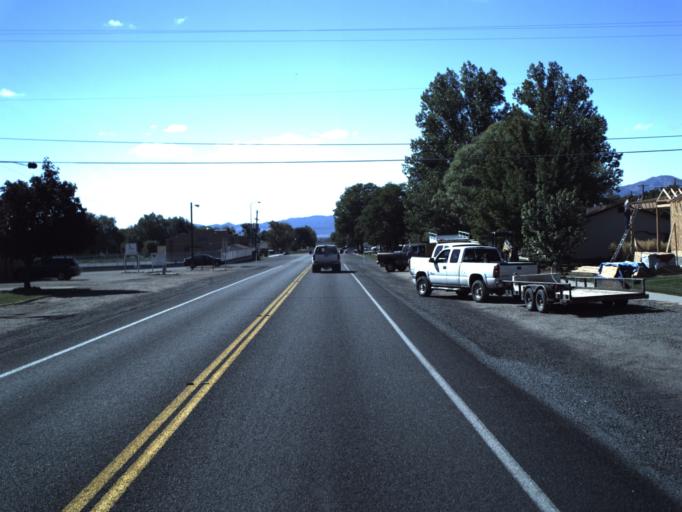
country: US
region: Utah
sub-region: Beaver County
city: Beaver
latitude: 38.2769
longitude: -112.6383
